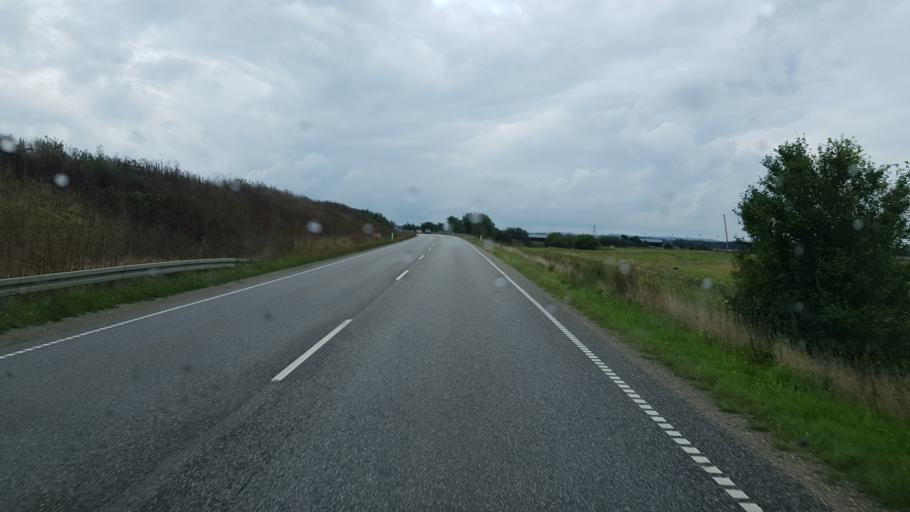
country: DK
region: Central Jutland
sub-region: Horsens Kommune
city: Horsens
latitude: 55.8930
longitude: 9.7599
